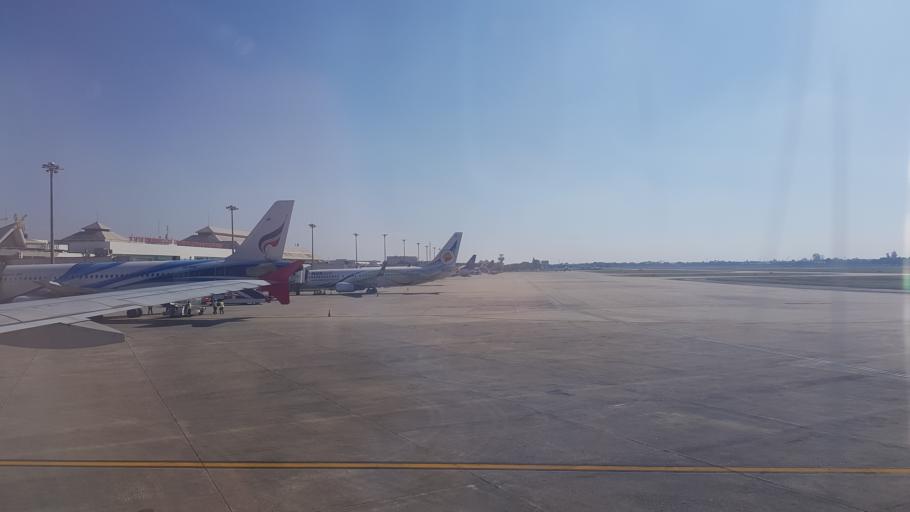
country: TH
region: Chiang Mai
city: Chiang Mai
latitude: 18.7704
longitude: 98.9670
